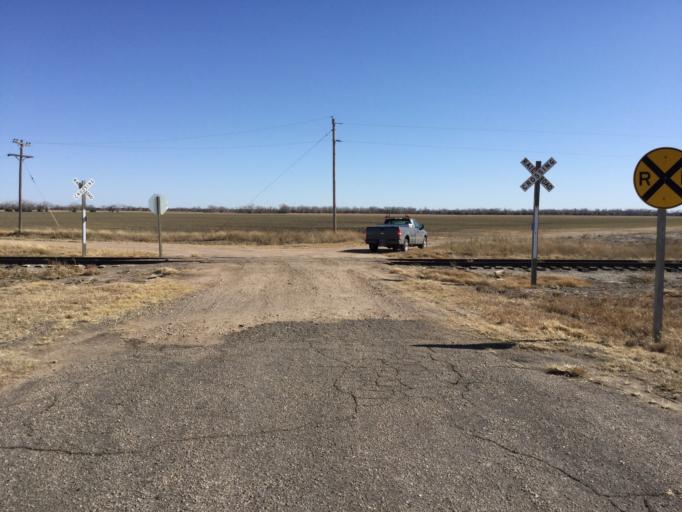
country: US
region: Kansas
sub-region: Pawnee County
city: Larned
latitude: 38.1018
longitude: -99.2053
